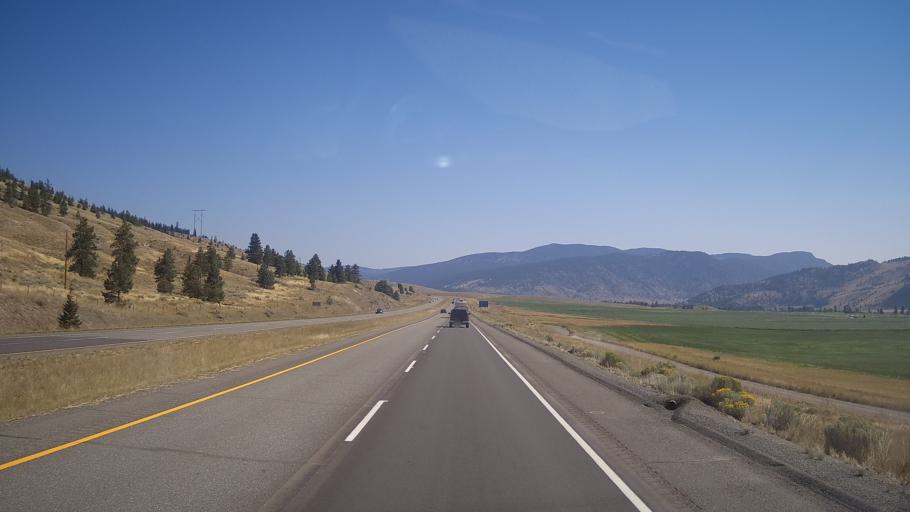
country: CA
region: British Columbia
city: Merritt
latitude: 50.1387
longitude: -120.7354
